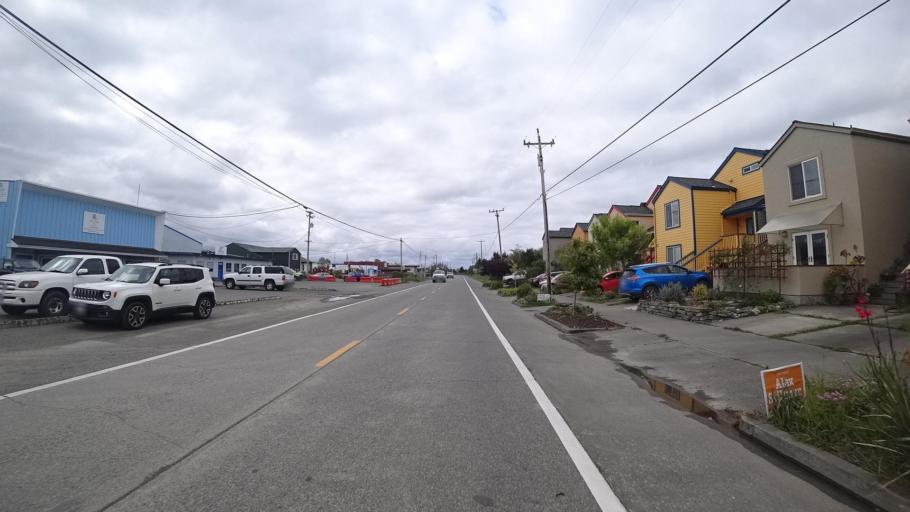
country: US
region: California
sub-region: Humboldt County
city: Arcata
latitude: 40.8609
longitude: -124.0888
